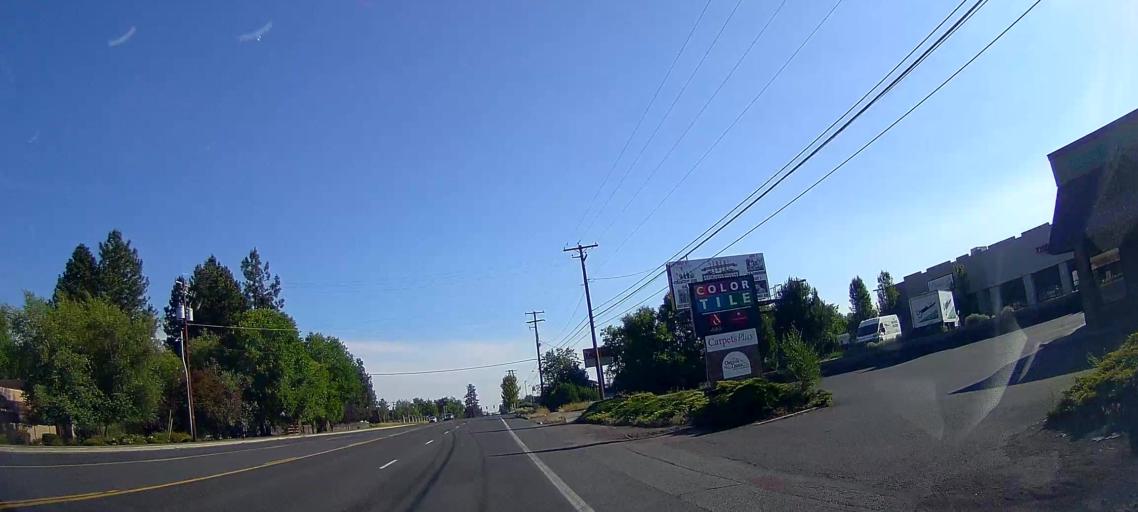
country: US
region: Oregon
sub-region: Deschutes County
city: Bend
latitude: 44.0884
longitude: -121.3060
